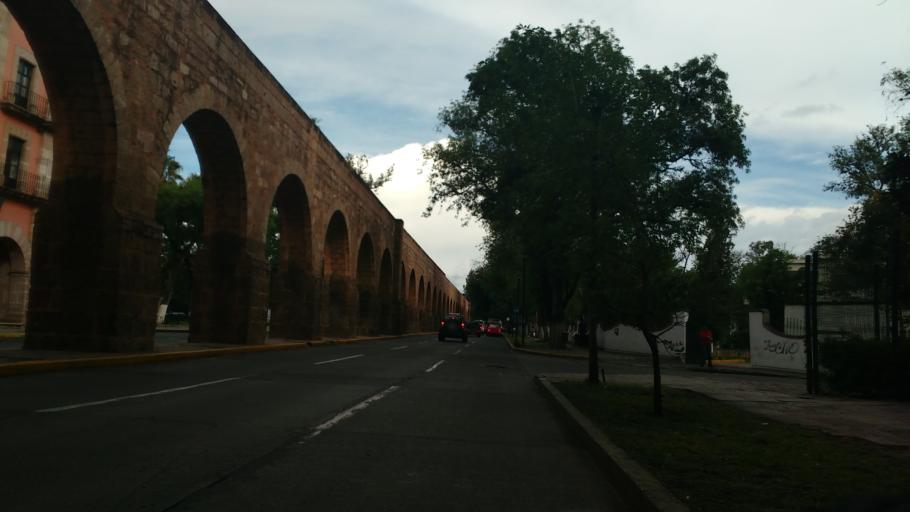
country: MX
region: Michoacan
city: Morelia
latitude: 19.7001
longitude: -101.1793
